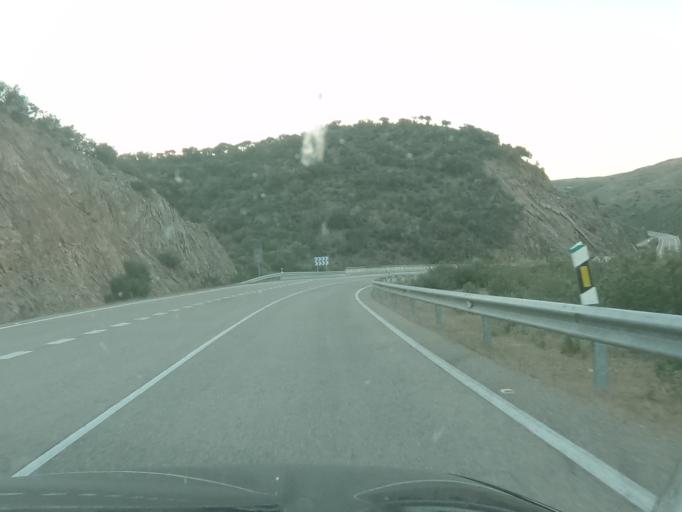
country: ES
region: Extremadura
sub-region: Provincia de Caceres
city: Salorino
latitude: 39.5704
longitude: -6.9982
